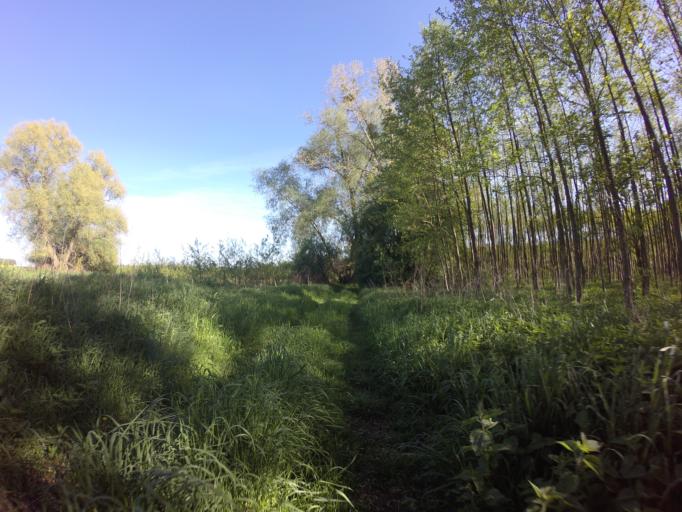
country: PL
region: West Pomeranian Voivodeship
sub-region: Powiat choszczenski
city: Pelczyce
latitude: 53.1361
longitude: 15.3182
